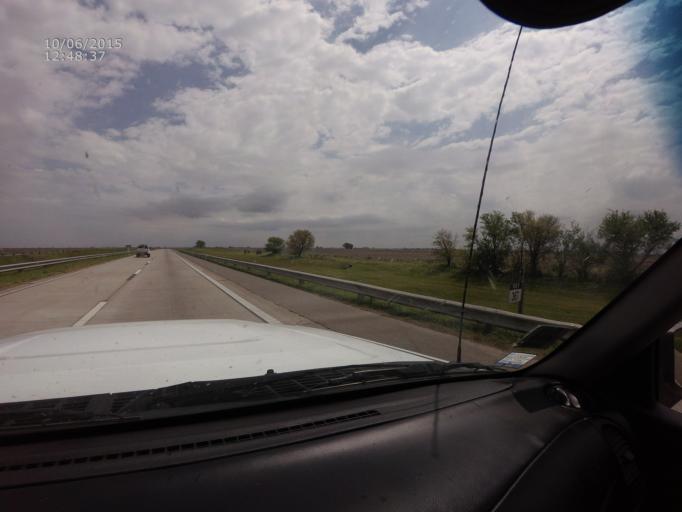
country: AR
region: Santa Fe
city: Canada de Gomez
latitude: -32.8371
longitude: -61.4534
